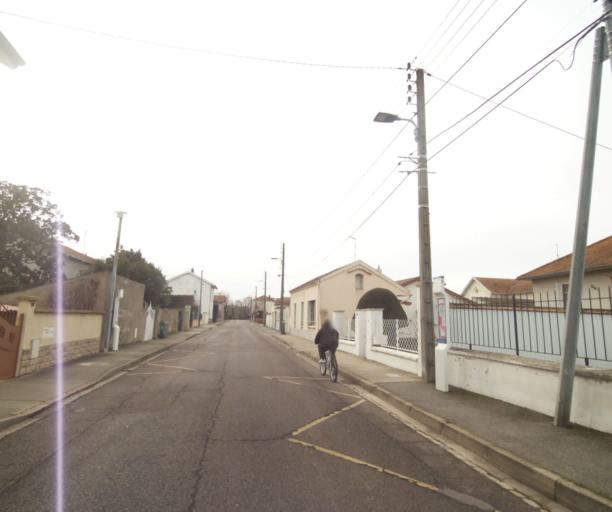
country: FR
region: Rhone-Alpes
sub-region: Departement de la Loire
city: Roanne
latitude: 46.0230
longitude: 4.0667
